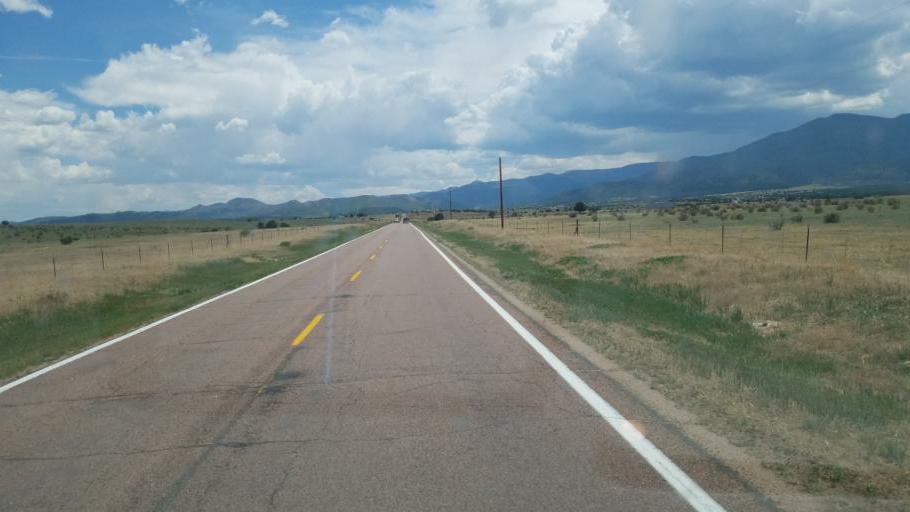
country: US
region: Colorado
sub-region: Fremont County
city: Florence
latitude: 38.2813
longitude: -105.0875
